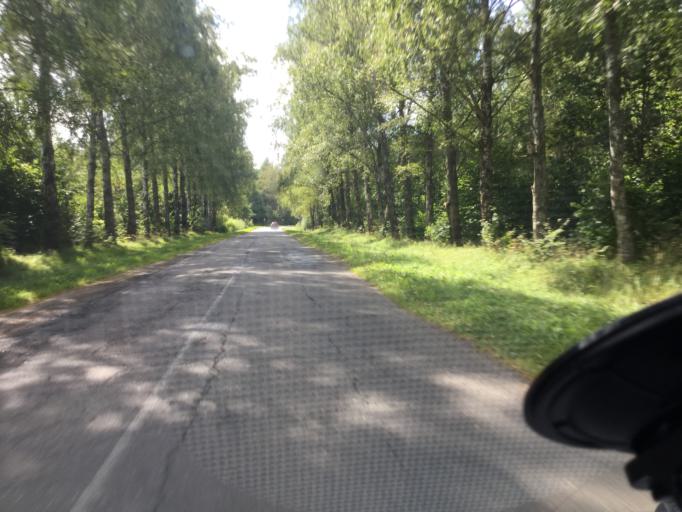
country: BY
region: Vitebsk
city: Chashniki
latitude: 55.3018
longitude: 29.3918
